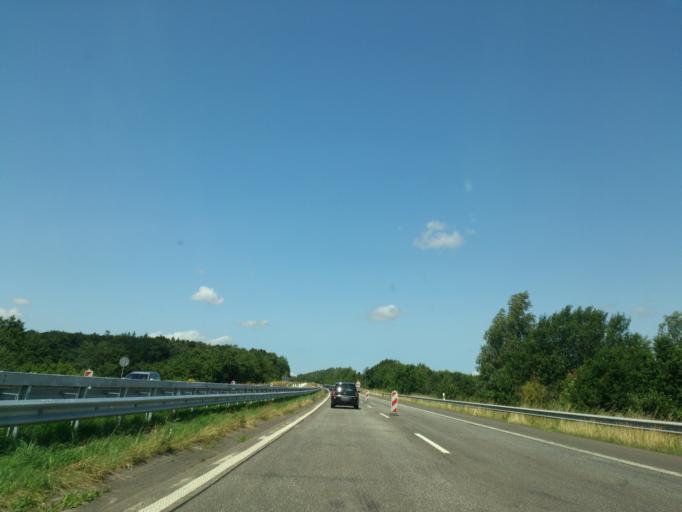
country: DE
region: Schleswig-Holstein
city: Arkebek
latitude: 54.1473
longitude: 9.2428
